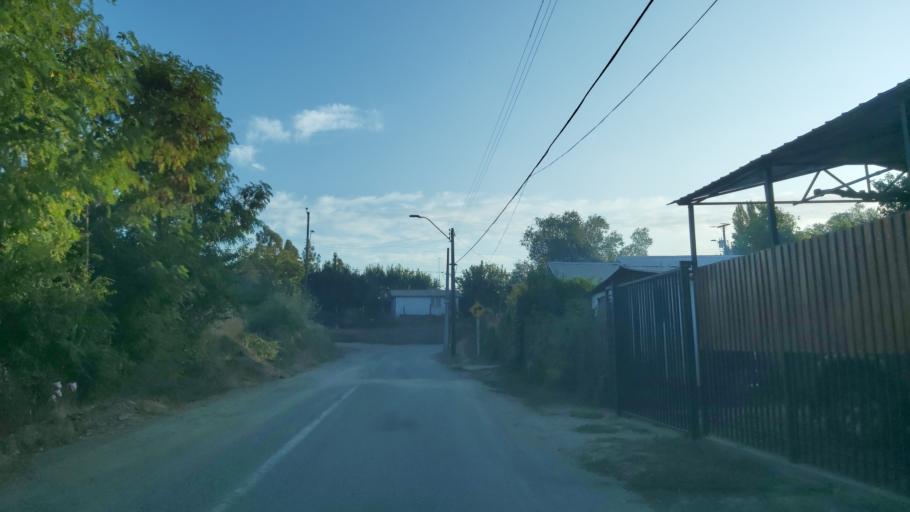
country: CL
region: Biobio
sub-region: Provincia de Biobio
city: La Laja
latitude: -37.1623
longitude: -72.9127
